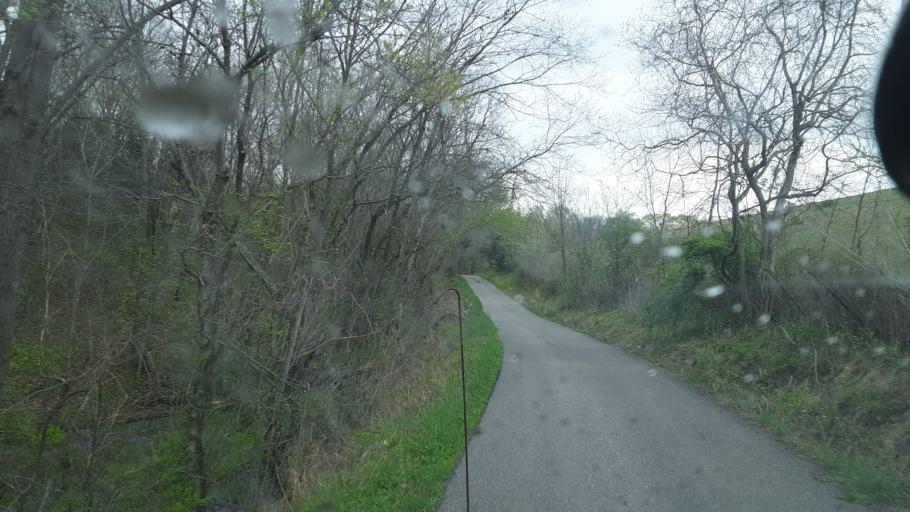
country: US
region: Kentucky
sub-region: Owen County
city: Owenton
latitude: 38.6423
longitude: -84.7801
